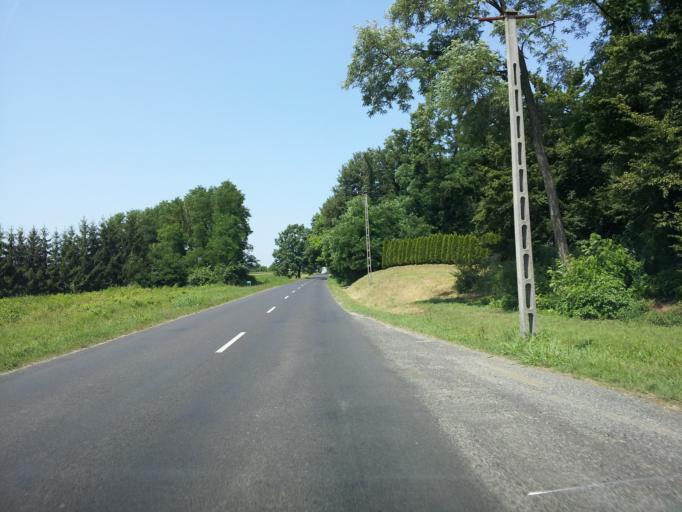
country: HU
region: Zala
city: Zalaegerszeg
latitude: 46.8595
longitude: 16.8156
